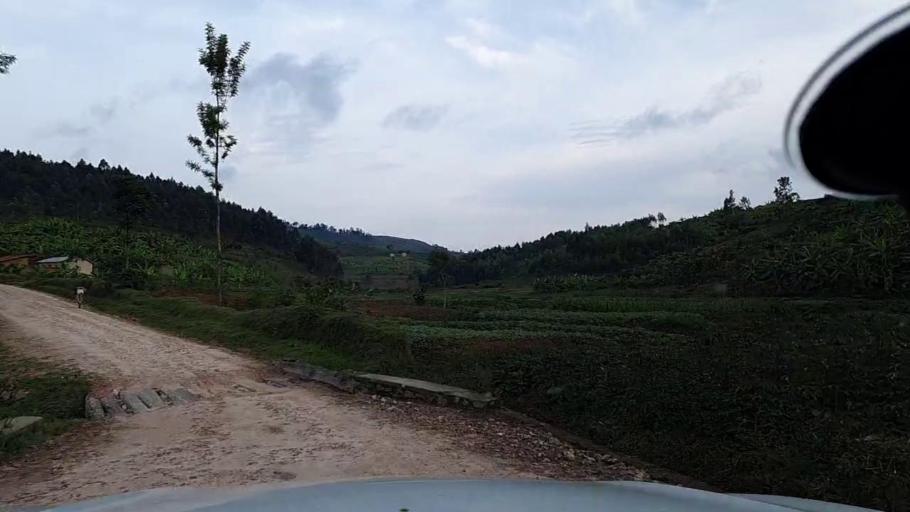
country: RW
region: Southern Province
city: Nyanza
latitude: -2.2150
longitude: 29.6253
